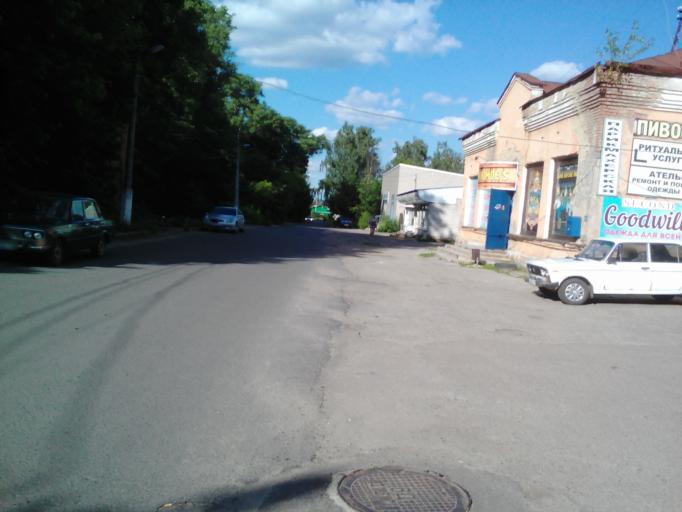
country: RU
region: Kursk
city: Voroshnevo
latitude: 51.6709
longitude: 36.0916
